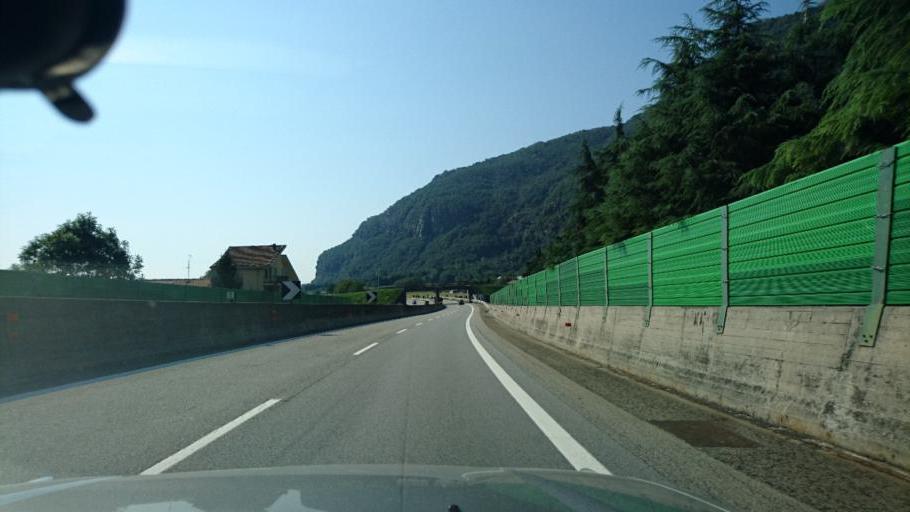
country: IT
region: Piedmont
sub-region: Provincia di Torino
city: Tavagnasco
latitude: 45.5465
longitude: 7.8240
